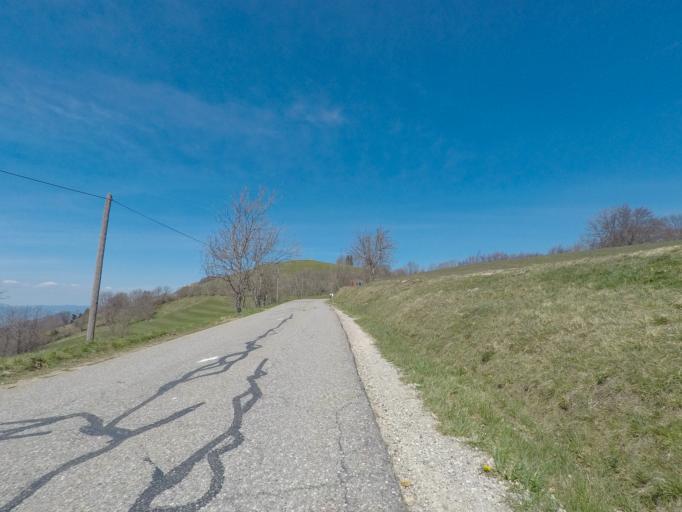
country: FR
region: Rhone-Alpes
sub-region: Departement de la Haute-Savoie
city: Collonges-sous-Saleve
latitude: 46.1240
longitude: 6.1714
